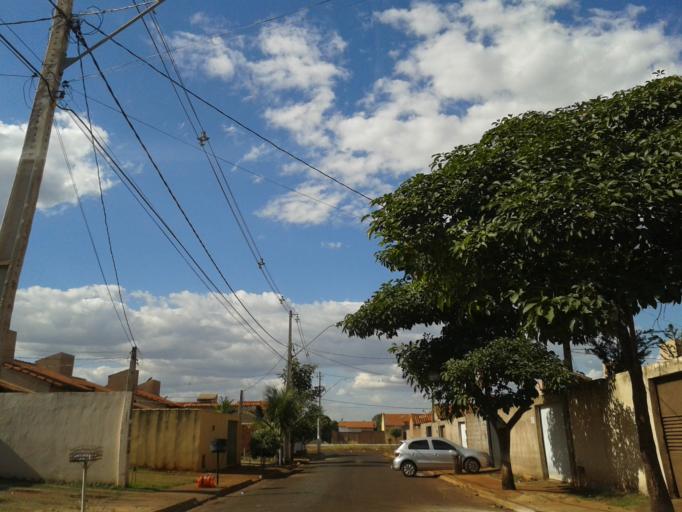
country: BR
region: Minas Gerais
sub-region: Capinopolis
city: Capinopolis
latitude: -18.6964
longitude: -49.5665
